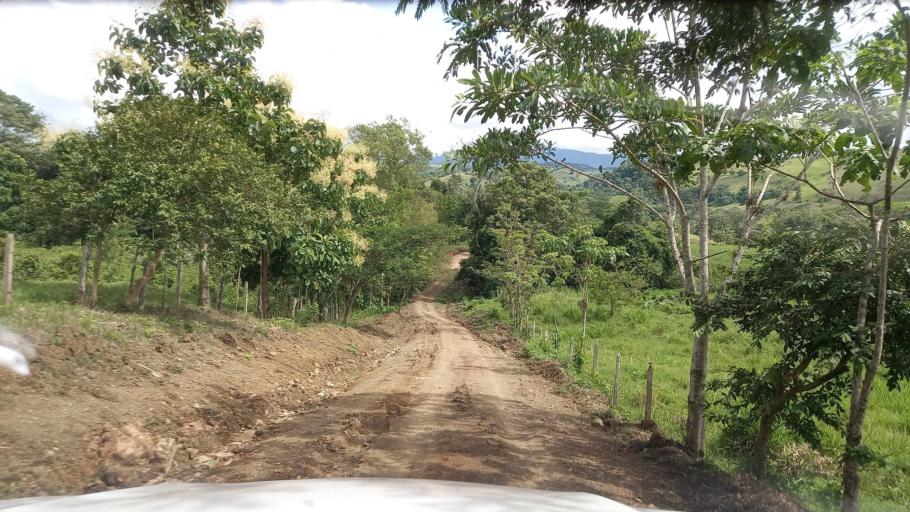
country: NI
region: Jinotega
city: San Jose de Bocay
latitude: 13.4112
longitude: -85.7026
